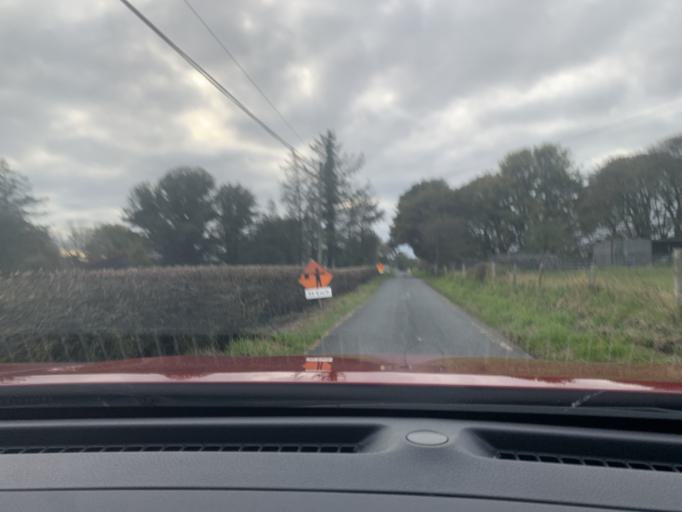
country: IE
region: Connaught
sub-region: Sligo
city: Tobercurry
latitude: 54.0295
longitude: -8.6653
